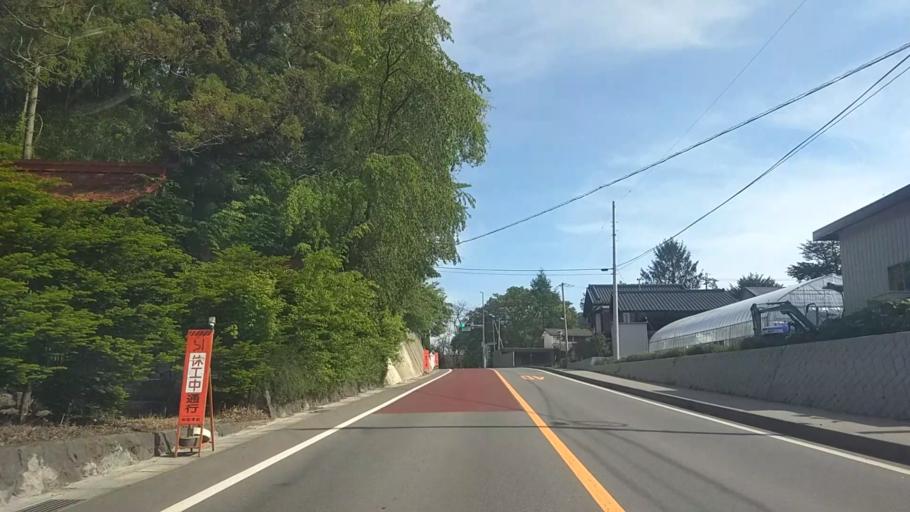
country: JP
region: Nagano
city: Saku
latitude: 36.0406
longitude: 138.4715
